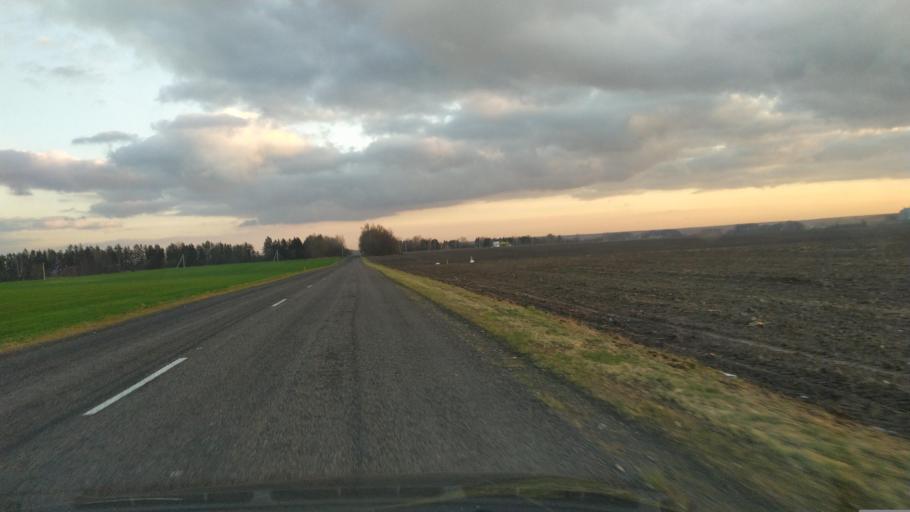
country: BY
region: Brest
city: Kamyanyets
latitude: 52.4170
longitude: 23.7819
